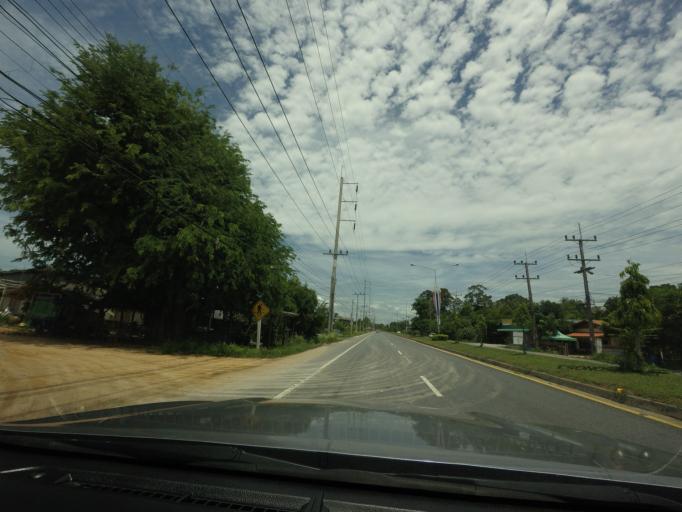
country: TH
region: Songkhla
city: Sathing Phra
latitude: 7.5571
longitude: 100.4138
